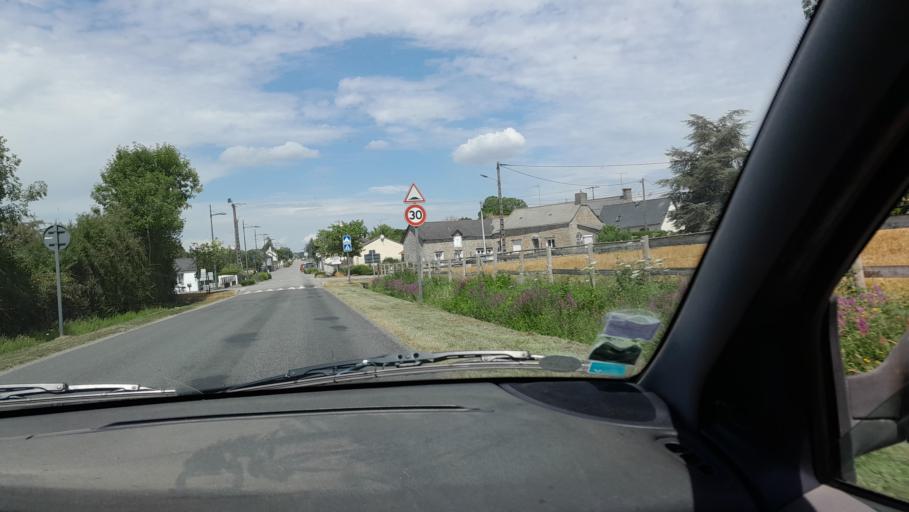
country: FR
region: Pays de la Loire
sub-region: Departement de la Mayenne
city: Saint-Pierre-la-Cour
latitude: 48.1042
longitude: -1.0214
